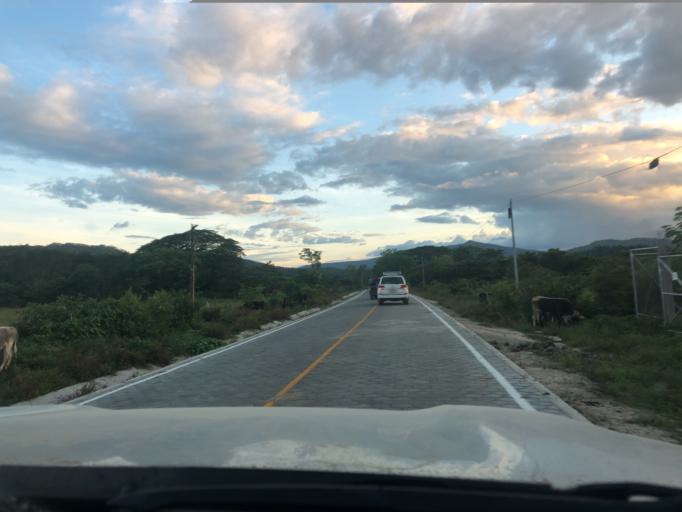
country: HN
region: El Paraiso
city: Santa Cruz
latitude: 13.7257
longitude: -86.6225
